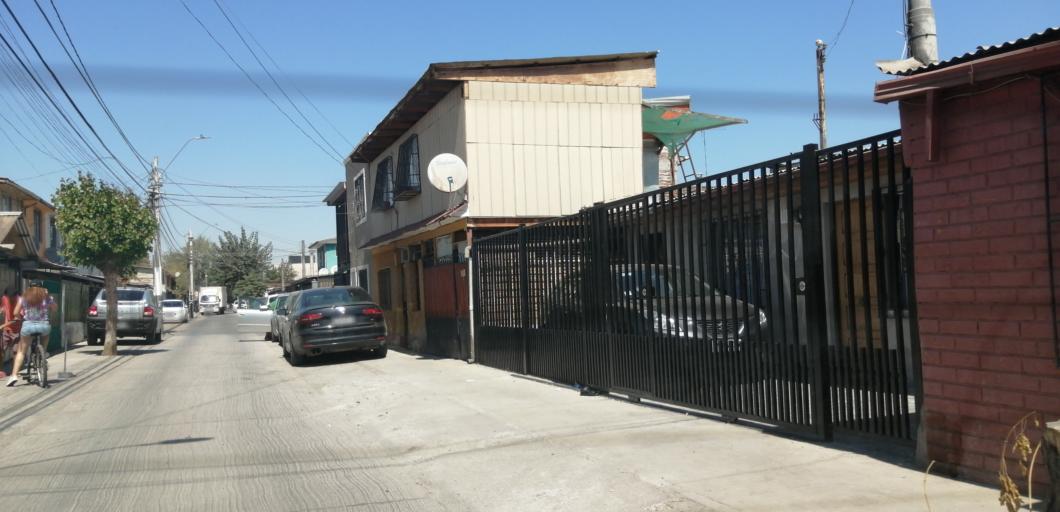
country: CL
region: Santiago Metropolitan
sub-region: Provincia de Santiago
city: Lo Prado
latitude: -33.4339
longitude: -70.7415
